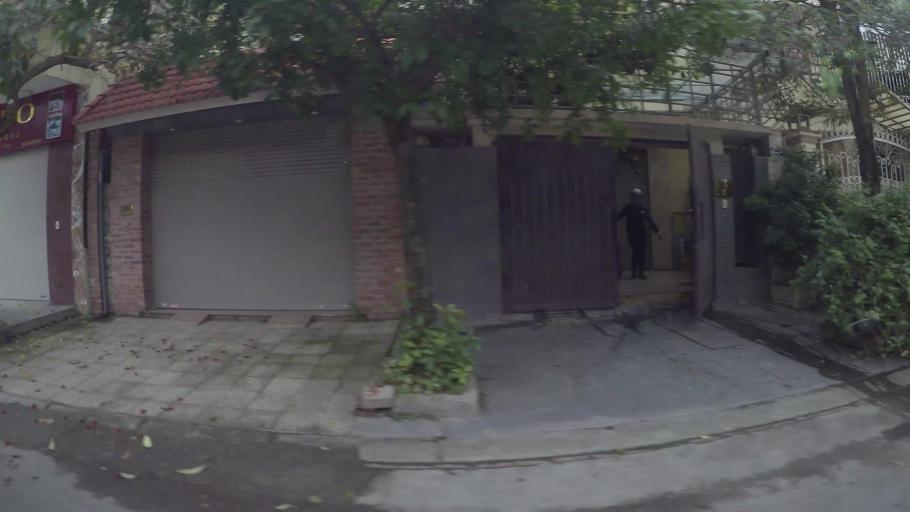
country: VN
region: Ha Noi
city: Hai BaTrung
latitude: 20.9861
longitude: 105.8680
